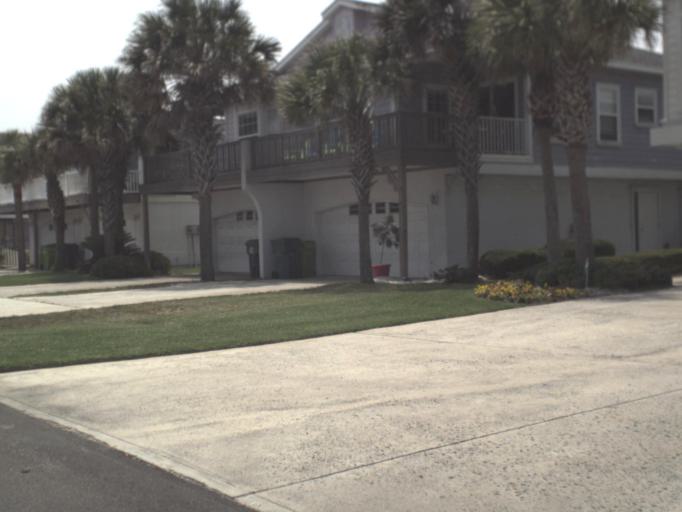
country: US
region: Florida
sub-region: Nassau County
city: Fernandina Beach
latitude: 30.6261
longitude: -81.4398
